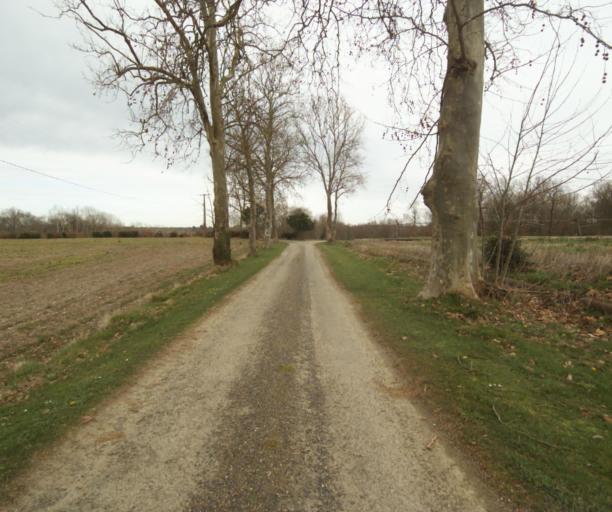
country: FR
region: Midi-Pyrenees
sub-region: Departement du Gers
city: Cazaubon
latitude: 43.9299
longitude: -0.0096
